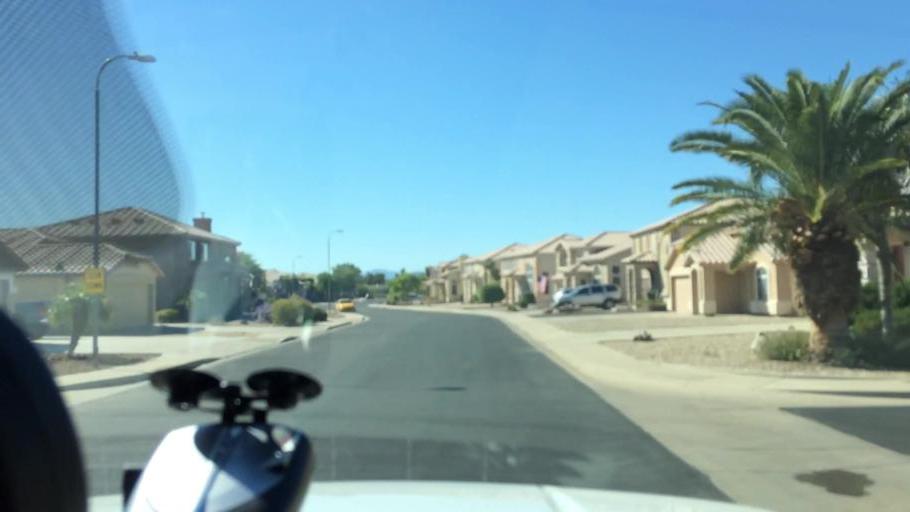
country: US
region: Arizona
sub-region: Maricopa County
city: Sun City
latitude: 33.5693
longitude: -112.2663
